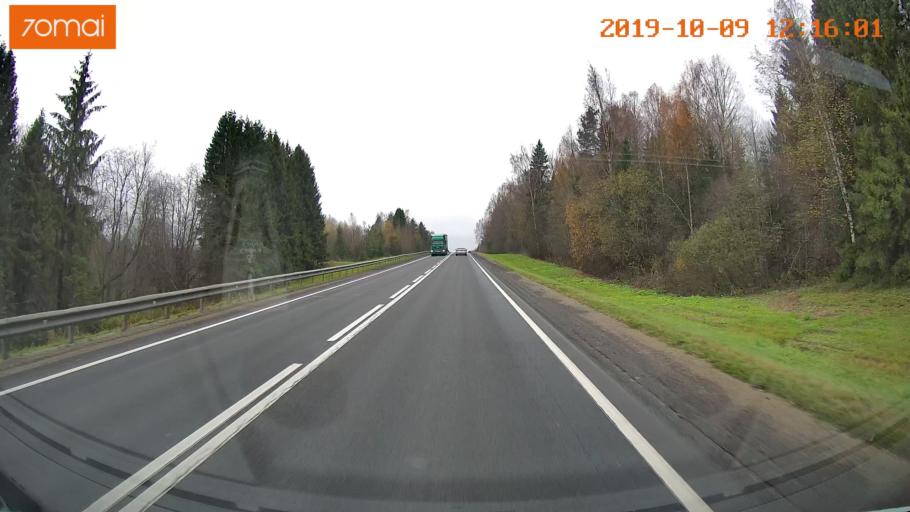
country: RU
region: Jaroslavl
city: Prechistoye
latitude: 58.4747
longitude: 40.3218
